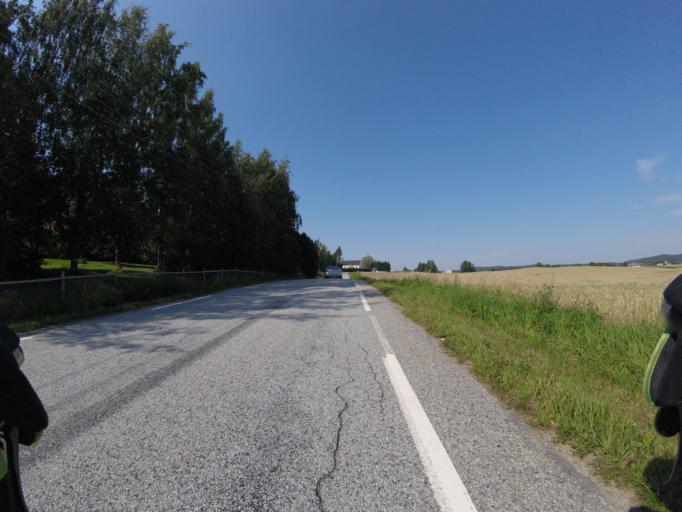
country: NO
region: Akershus
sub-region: Ullensaker
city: Klofta
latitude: 60.0854
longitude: 11.1632
